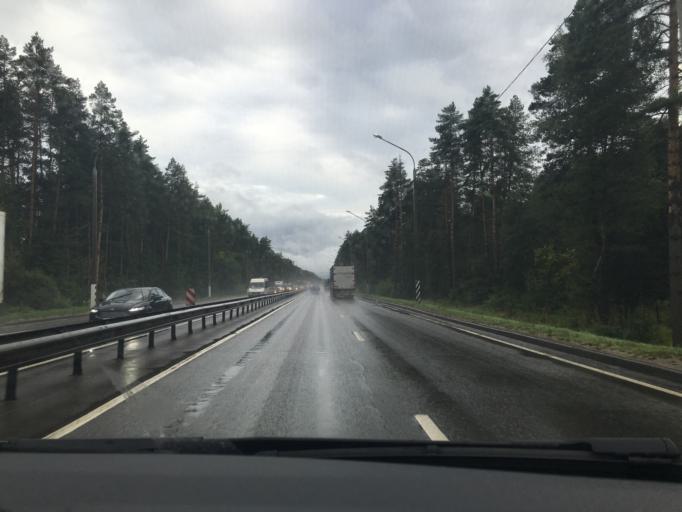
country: RU
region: Kaluga
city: Obninsk
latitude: 55.0645
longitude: 36.6225
